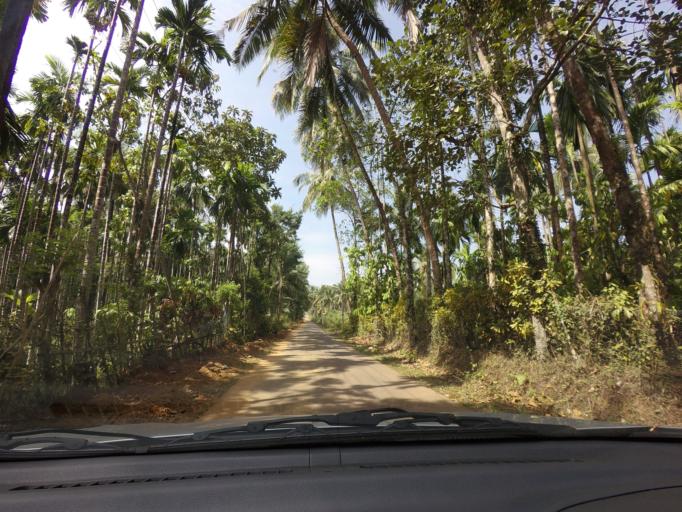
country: IN
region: Karnataka
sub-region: Kodagu
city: Somvarpet
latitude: 12.6867
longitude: 75.6126
